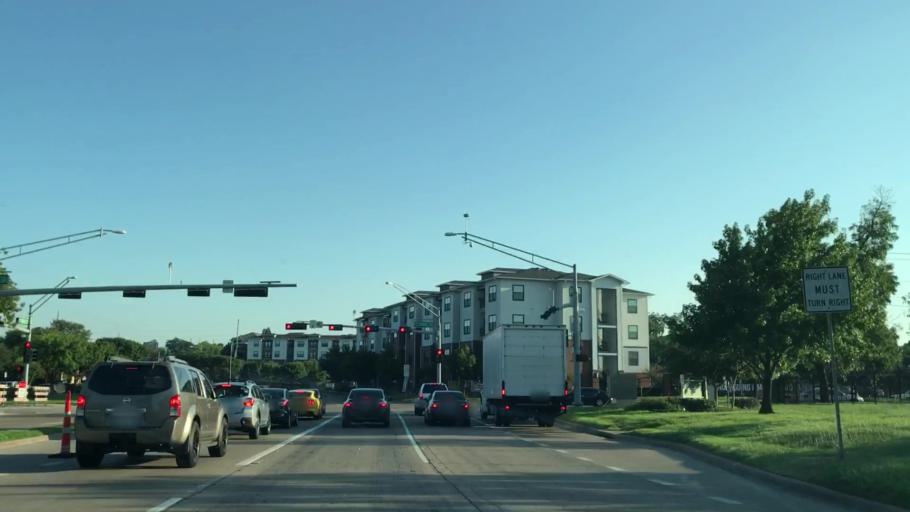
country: US
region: Texas
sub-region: Denton County
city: Denton
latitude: 33.2071
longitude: -97.1368
